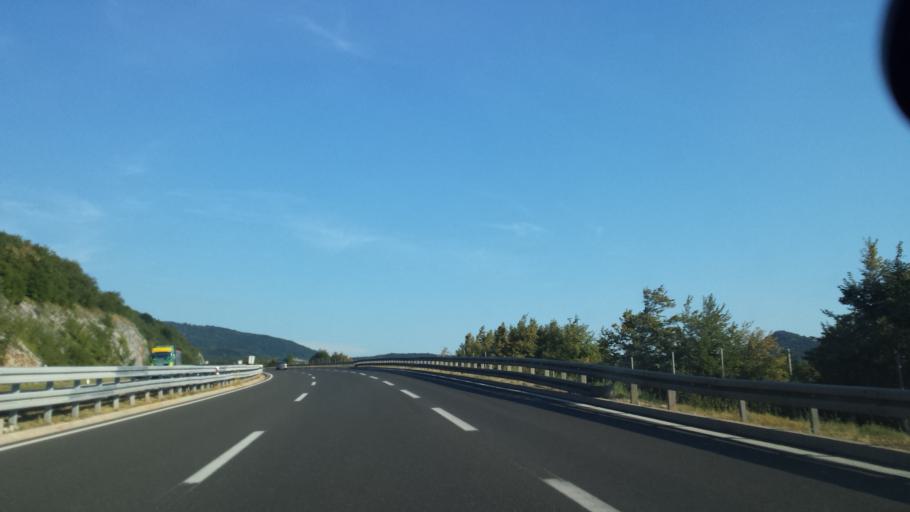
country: HR
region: Primorsko-Goranska
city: Krasica
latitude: 45.3568
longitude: 14.5784
